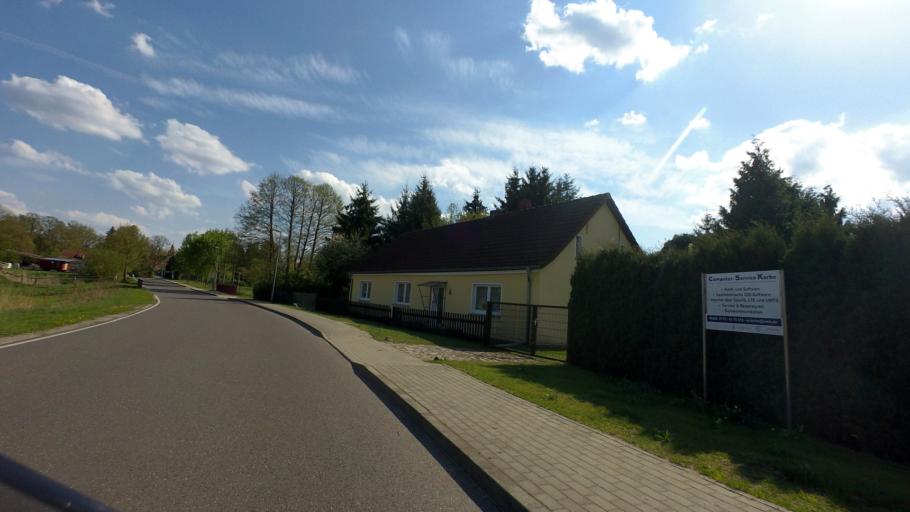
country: DE
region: Brandenburg
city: Templin
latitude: 53.0545
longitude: 13.5265
